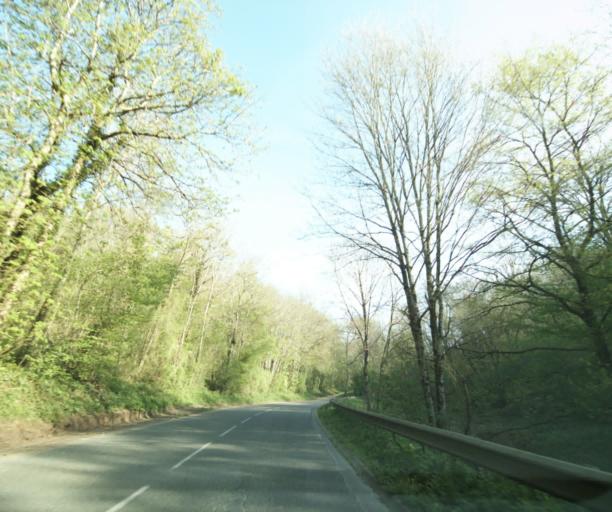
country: FR
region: Ile-de-France
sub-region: Departement de Seine-et-Marne
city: Vernou-la-Celle-sur-Seine
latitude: 48.4000
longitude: 2.8316
